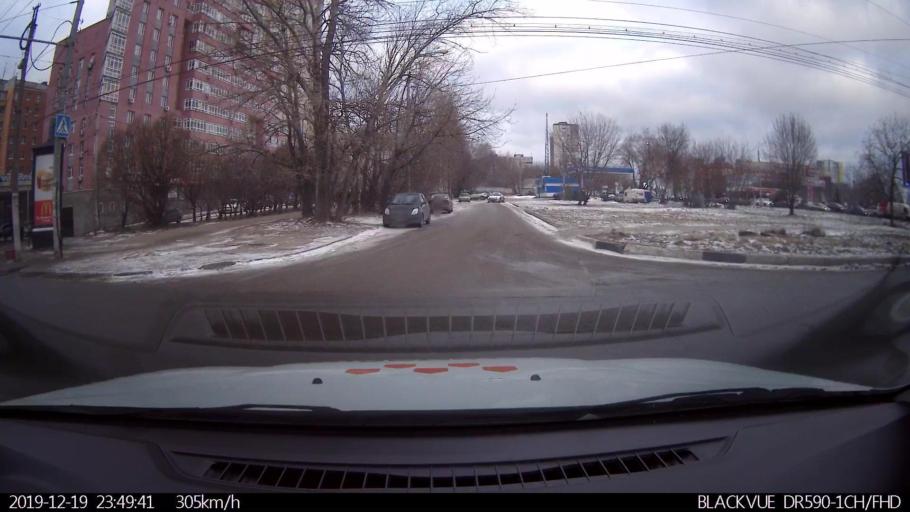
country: RU
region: Jaroslavl
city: Breytovo
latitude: 58.4212
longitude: 37.9481
